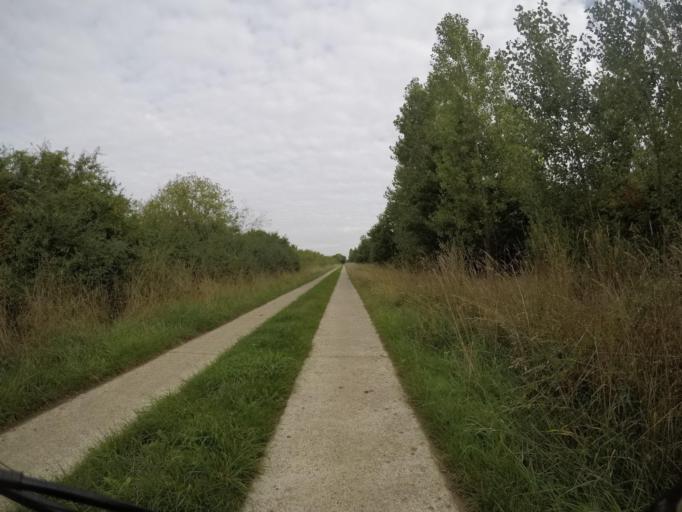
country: DE
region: Lower Saxony
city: Neu Darchau
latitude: 53.3084
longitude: 10.8726
